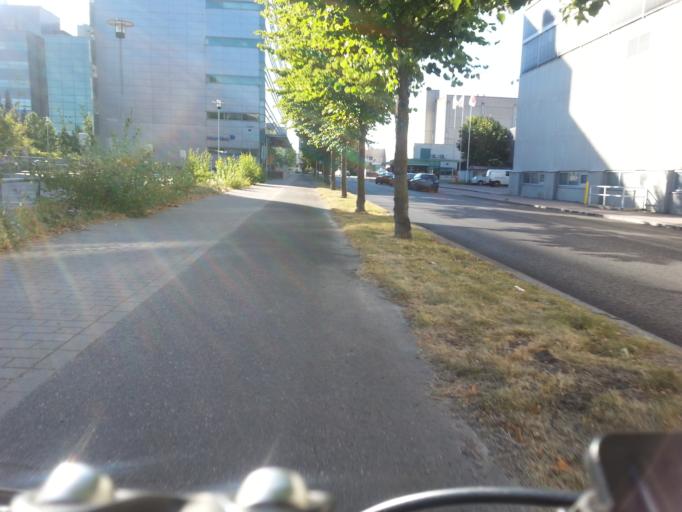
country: FI
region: Uusimaa
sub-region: Helsinki
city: Teekkarikylae
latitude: 60.2199
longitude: 24.8735
